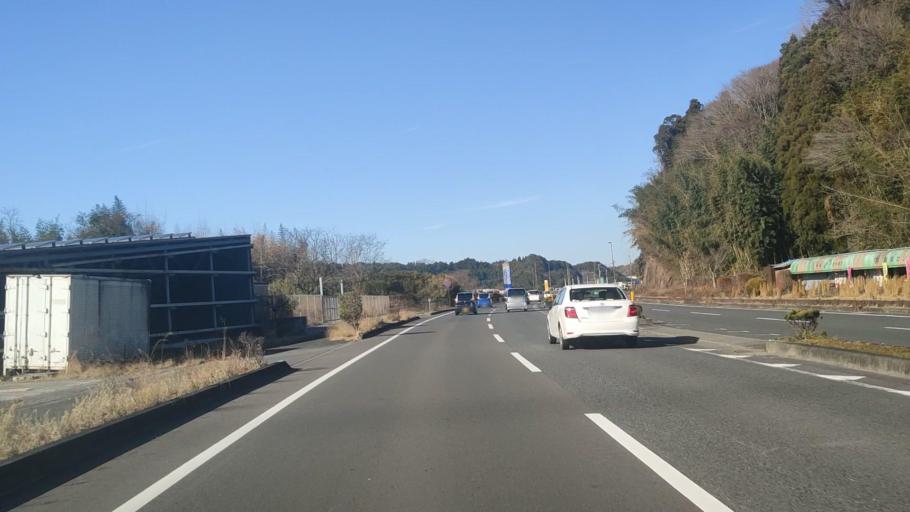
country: JP
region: Oita
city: Oita
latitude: 33.1153
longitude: 131.6543
